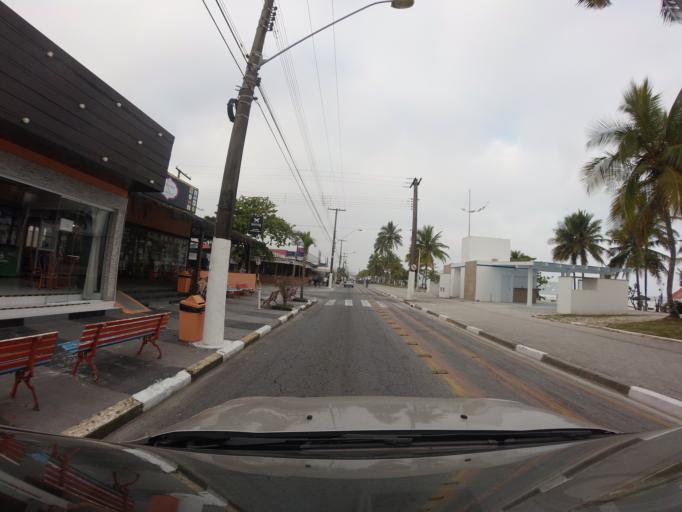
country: BR
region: Sao Paulo
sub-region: Guaruja
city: Guaruja
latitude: -23.9879
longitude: -46.2345
